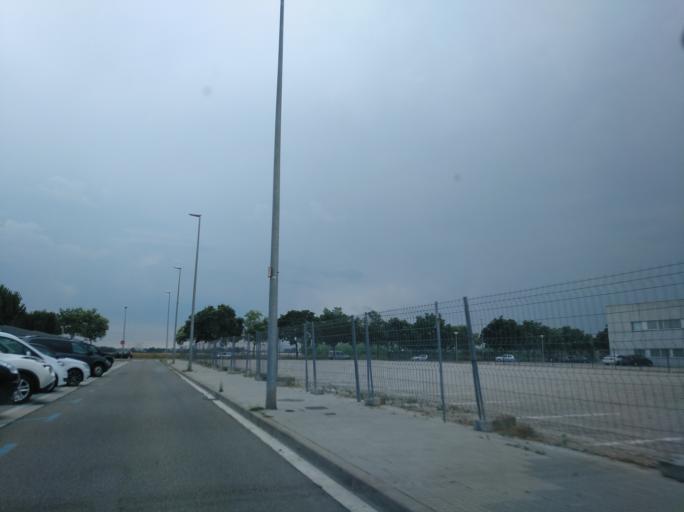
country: ES
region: Catalonia
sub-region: Provincia de Girona
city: Salt
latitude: 41.9694
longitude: 2.7945
